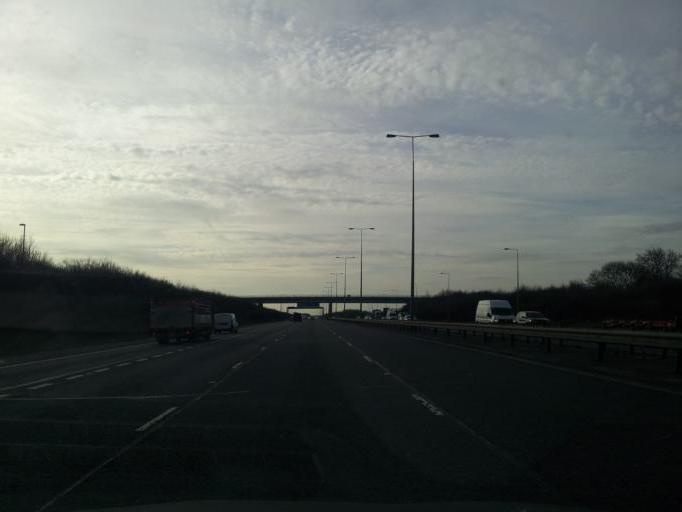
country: GB
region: England
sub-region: Cambridgeshire
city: Great Stukeley
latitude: 52.3883
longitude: -0.2586
